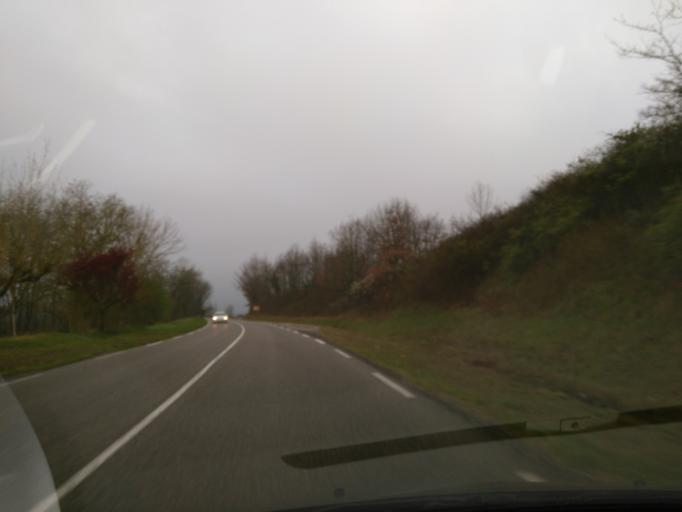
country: FR
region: Aquitaine
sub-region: Departement du Lot-et-Garonne
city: Bias
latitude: 44.4784
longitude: 0.6801
